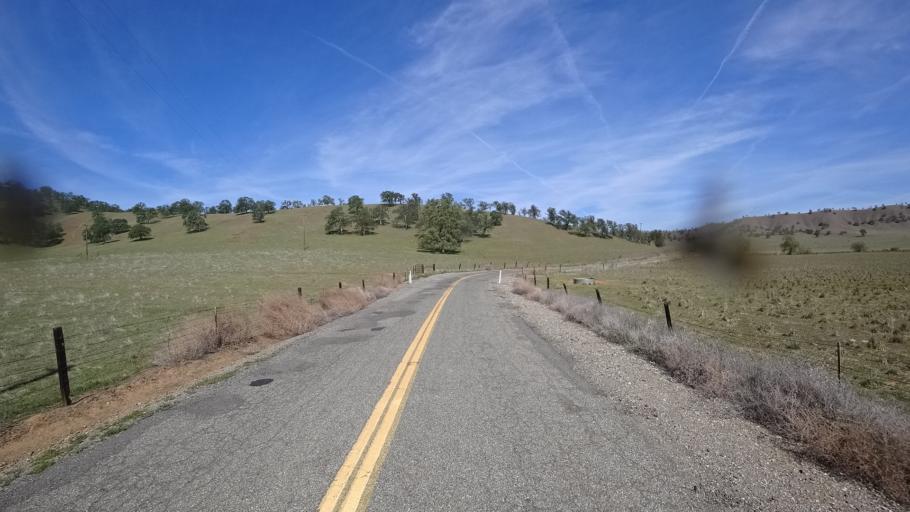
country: US
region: California
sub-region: Glenn County
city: Willows
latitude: 39.5452
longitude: -122.4300
